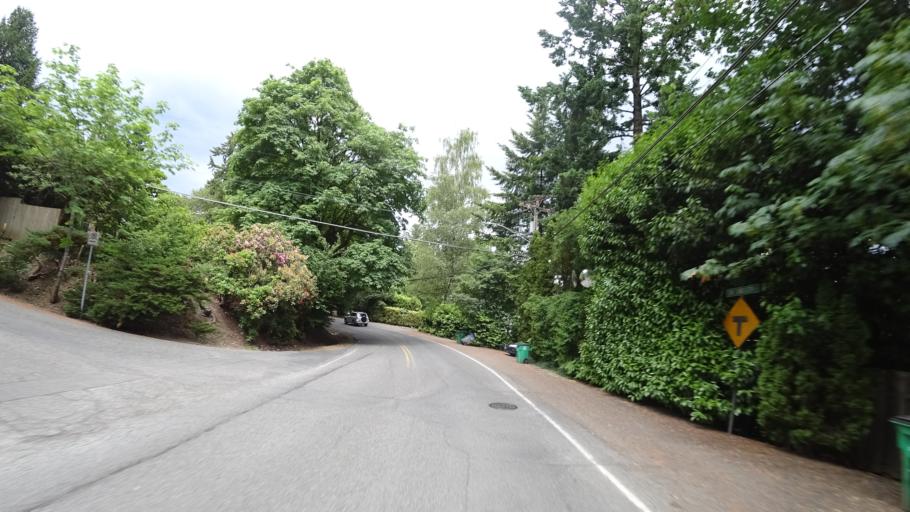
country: US
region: Oregon
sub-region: Clackamas County
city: Lake Oswego
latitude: 45.4543
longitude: -122.7004
